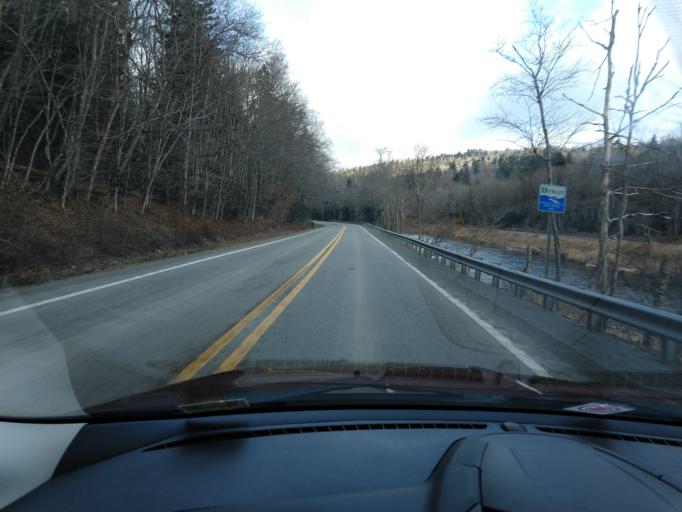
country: US
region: West Virginia
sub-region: Randolph County
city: Elkins
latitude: 38.6294
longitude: -79.8733
